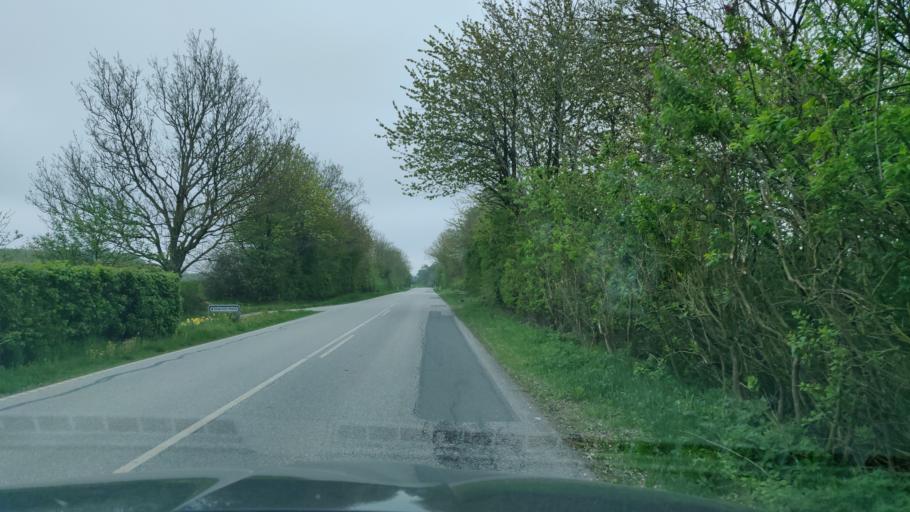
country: DK
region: South Denmark
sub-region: Sonderborg Kommune
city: Guderup
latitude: 55.0011
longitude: 9.9439
